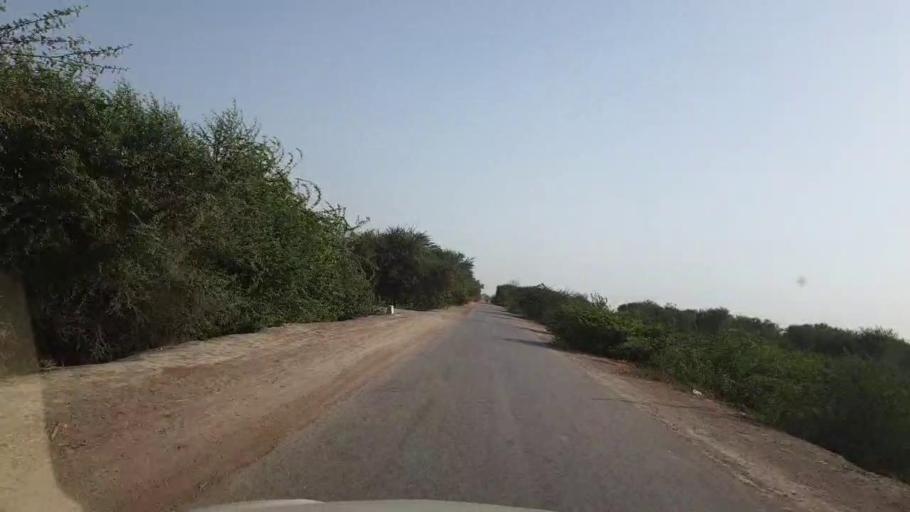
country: PK
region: Sindh
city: Tando Ghulam Ali
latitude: 25.0984
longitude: 68.8689
